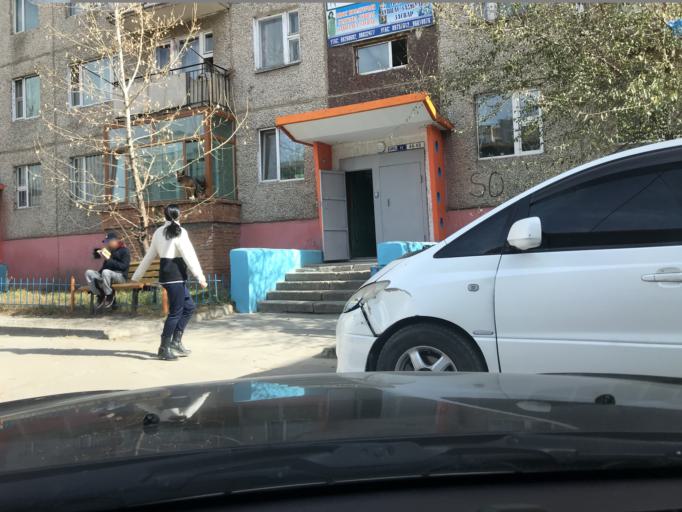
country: MN
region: Ulaanbaatar
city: Ulaanbaatar
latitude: 47.9215
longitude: 106.9444
